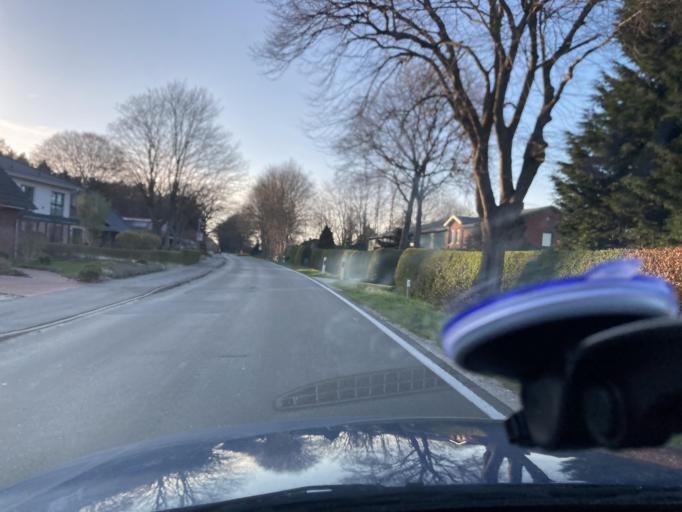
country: DE
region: Schleswig-Holstein
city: Suderheistedt
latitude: 54.2232
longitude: 9.1192
